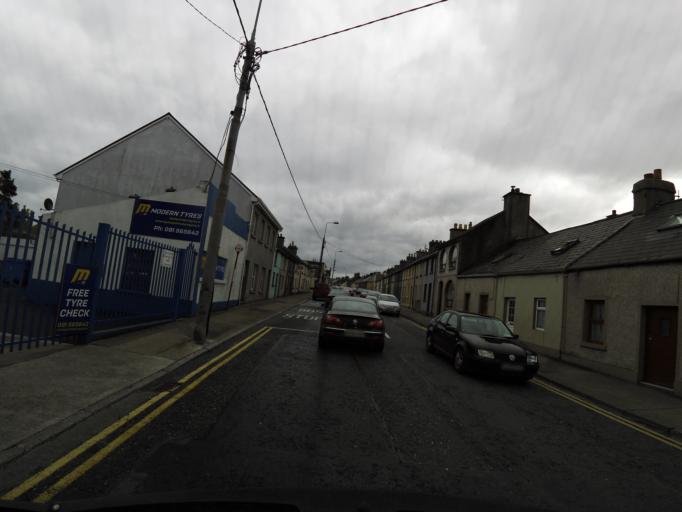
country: IE
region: Connaught
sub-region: County Galway
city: Gaillimh
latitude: 53.2791
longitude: -9.0444
